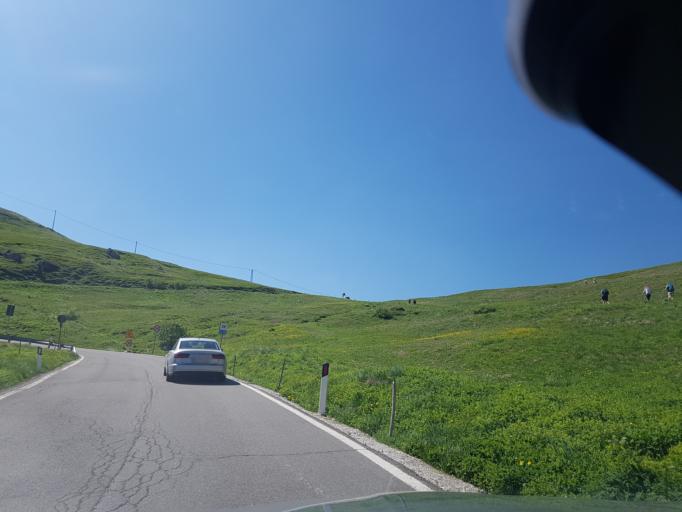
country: IT
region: Trentino-Alto Adige
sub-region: Provincia di Trento
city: Canazei
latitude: 46.5084
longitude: 11.7569
